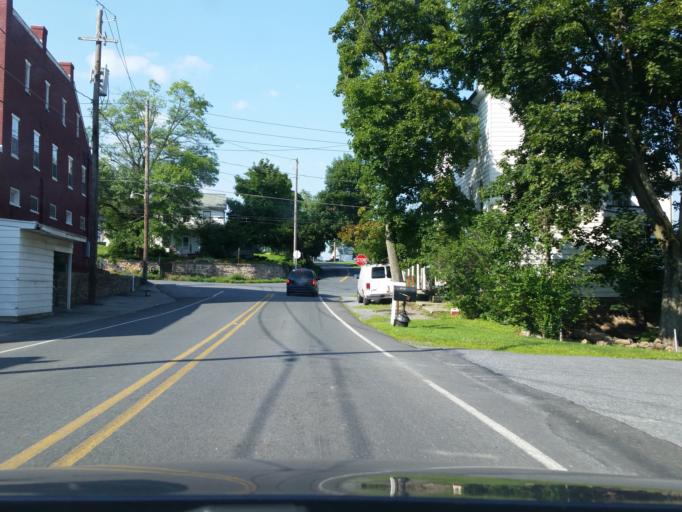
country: US
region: Pennsylvania
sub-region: Lancaster County
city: Mount Joy
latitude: 40.1965
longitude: -76.4875
